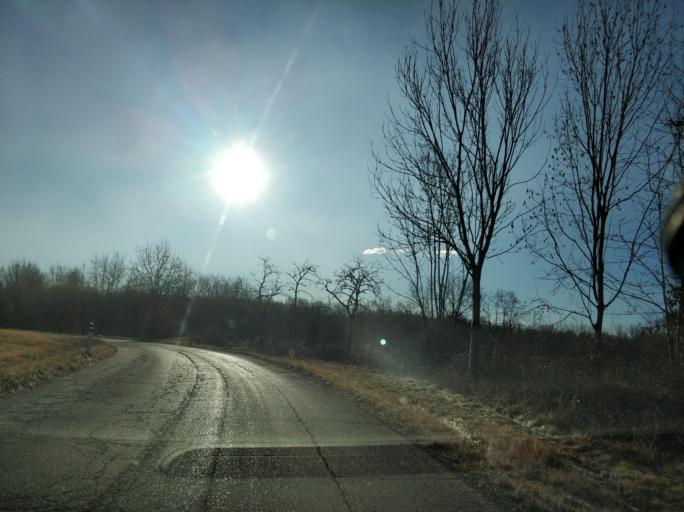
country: IT
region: Piedmont
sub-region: Provincia di Torino
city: Vauda Canavese Superiore
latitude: 45.2649
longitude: 7.6399
